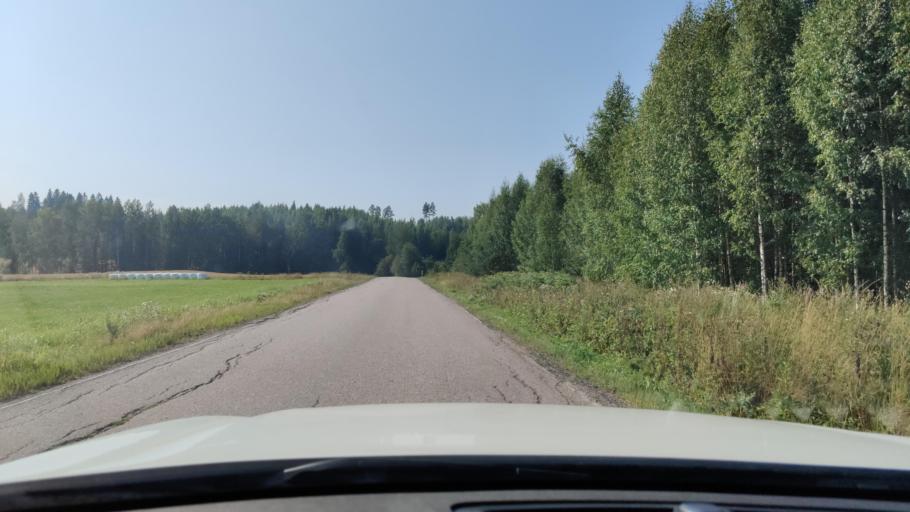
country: FI
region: Haeme
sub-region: Riihimaeki
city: Riihimaeki
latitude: 60.7169
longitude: 24.6992
